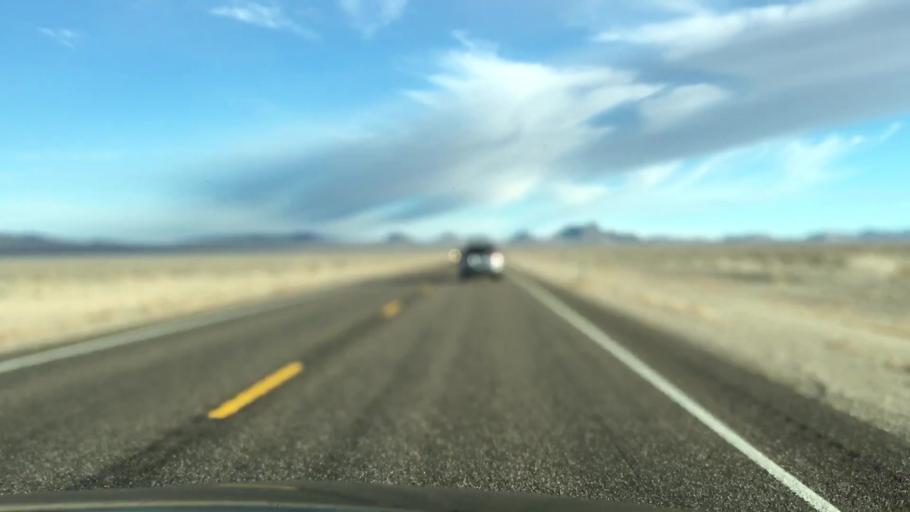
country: US
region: Nevada
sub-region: Nye County
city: Tonopah
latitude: 38.1241
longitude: -117.4040
